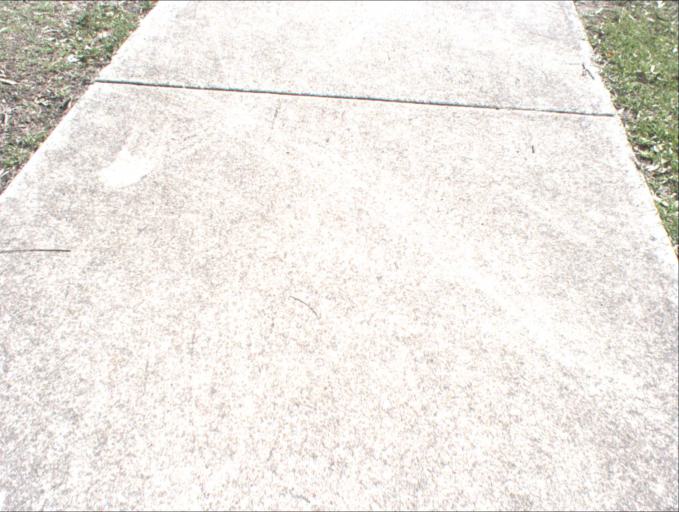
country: AU
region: Queensland
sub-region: Logan
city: Waterford West
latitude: -27.7121
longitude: 153.1551
